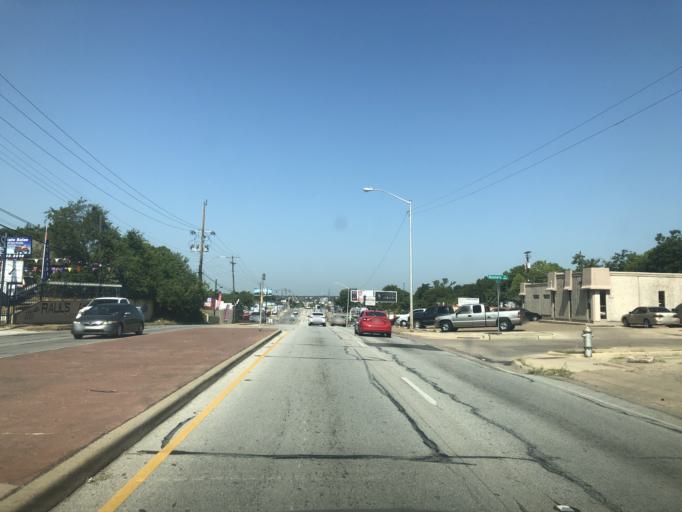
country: US
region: Texas
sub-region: Tarrant County
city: Haltom City
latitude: 32.7953
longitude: -97.3277
